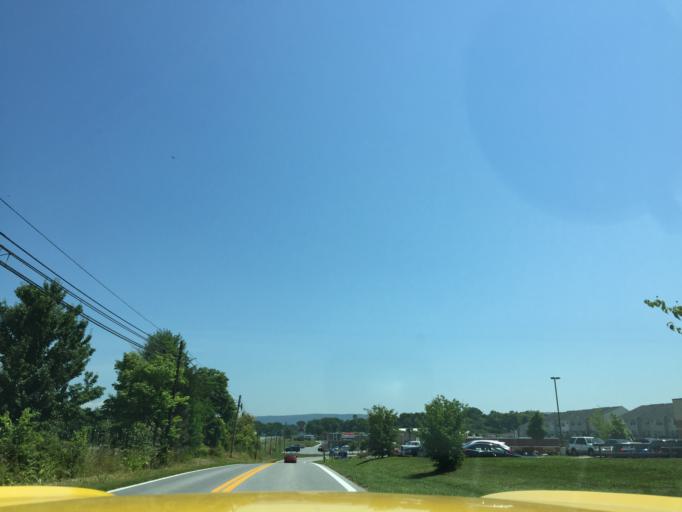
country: US
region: West Virginia
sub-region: Jefferson County
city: Ranson
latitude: 39.3015
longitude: -77.8199
